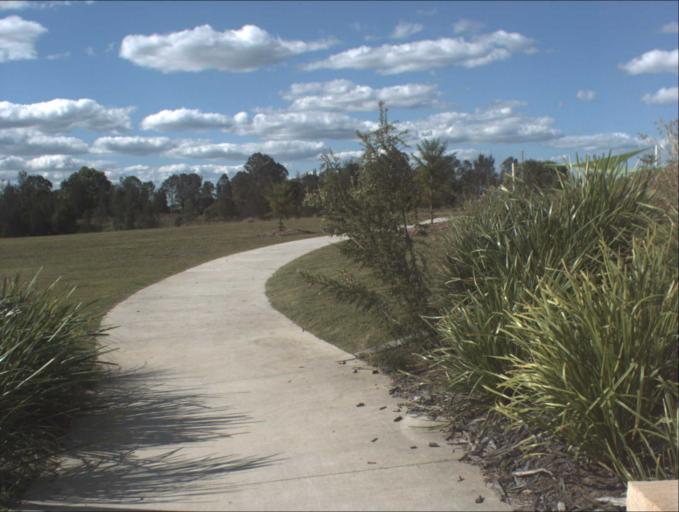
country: AU
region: Queensland
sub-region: Logan
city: Chambers Flat
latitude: -27.7755
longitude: 153.0975
